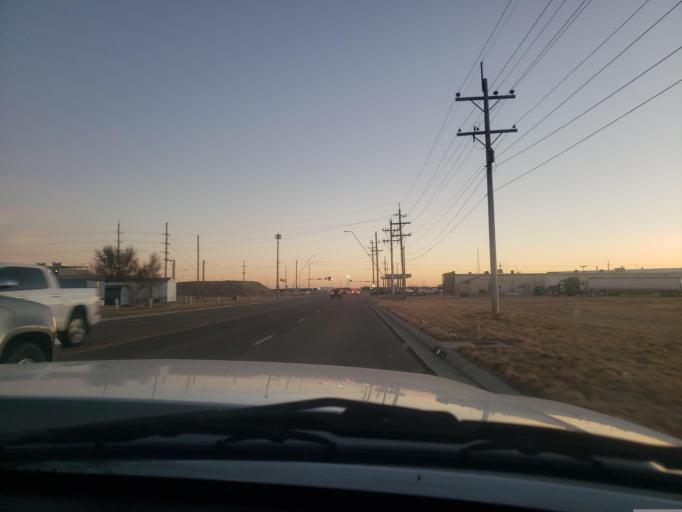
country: US
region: Kansas
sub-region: Finney County
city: Garden City
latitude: 37.9623
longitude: -100.8291
